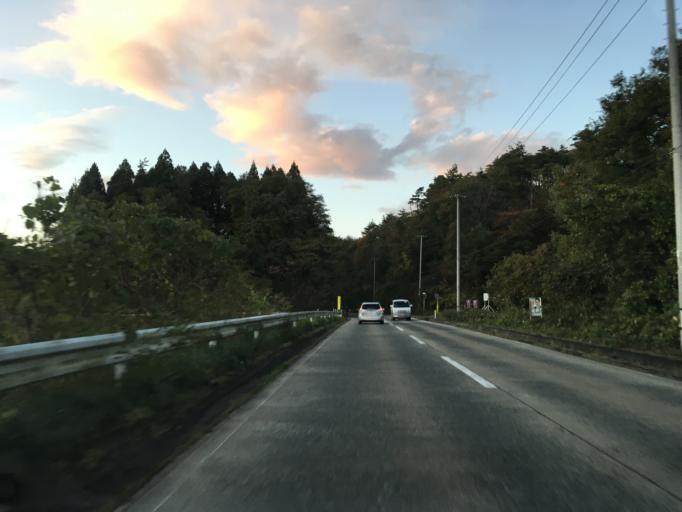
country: JP
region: Iwate
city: Kitakami
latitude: 39.2931
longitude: 141.2122
